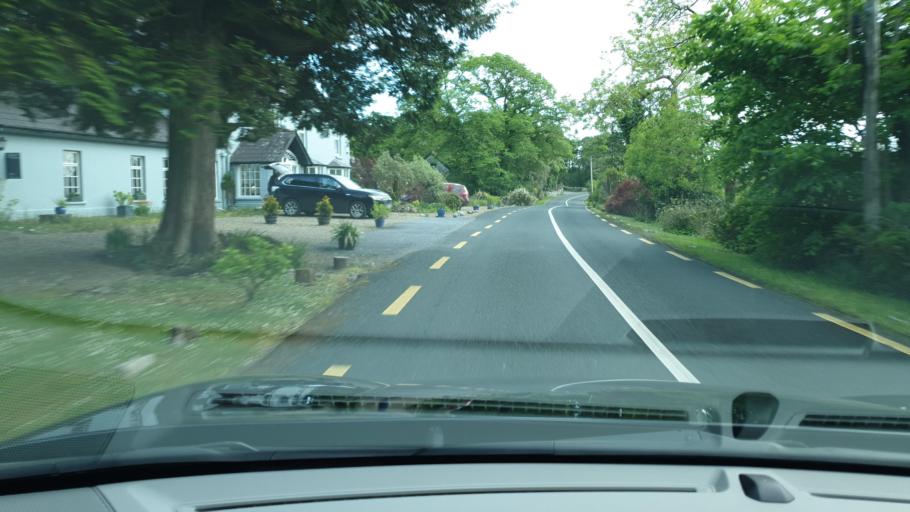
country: IE
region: Connaught
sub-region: County Galway
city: Clifden
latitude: 53.4391
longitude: -9.8683
